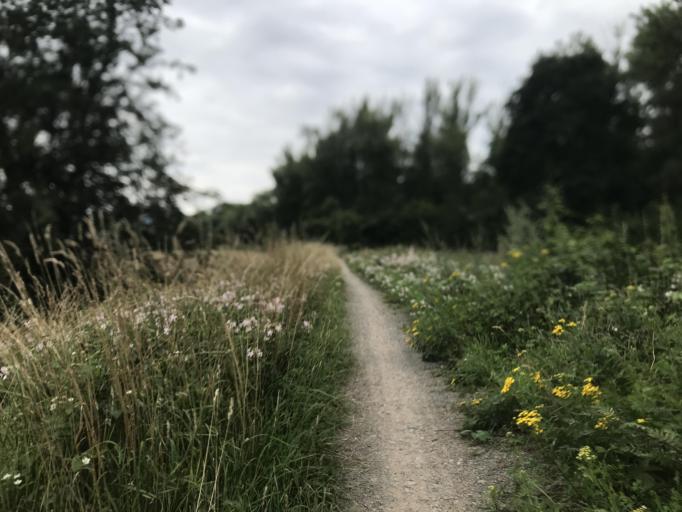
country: DE
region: Saxony-Anhalt
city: Weddersleben
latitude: 51.7659
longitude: 11.0970
